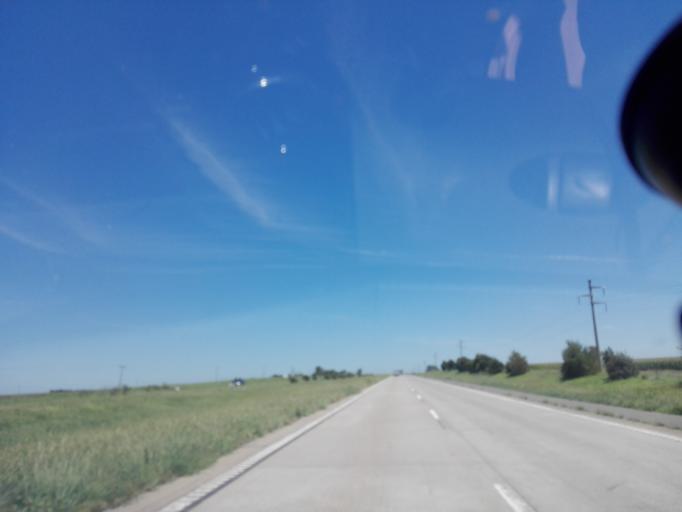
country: AR
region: Santa Fe
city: Canada de Gomez
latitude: -32.8508
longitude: -61.3654
